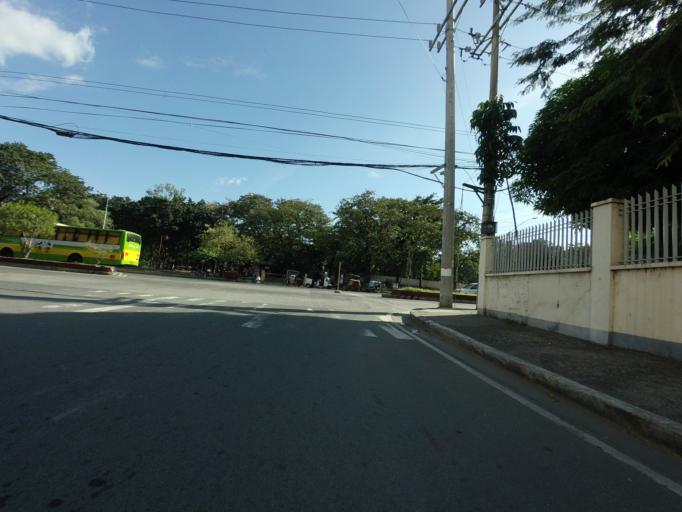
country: PH
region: Metro Manila
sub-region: City of Manila
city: Quiapo
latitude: 14.5950
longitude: 120.9784
